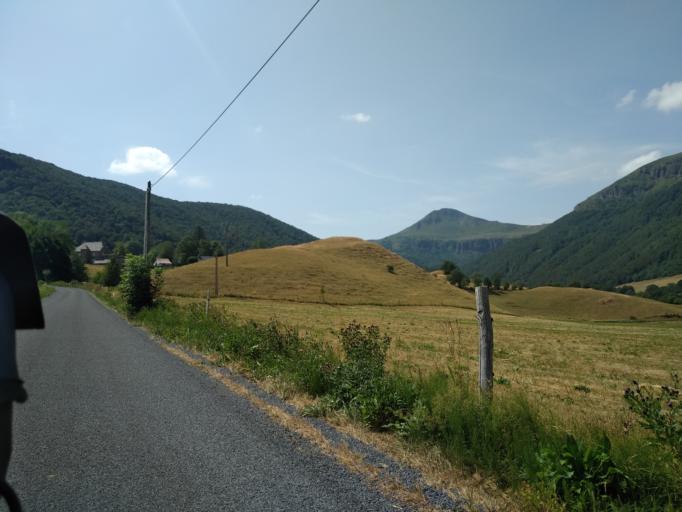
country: FR
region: Auvergne
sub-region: Departement du Cantal
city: Riom-es-Montagnes
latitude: 45.1393
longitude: 2.6971
